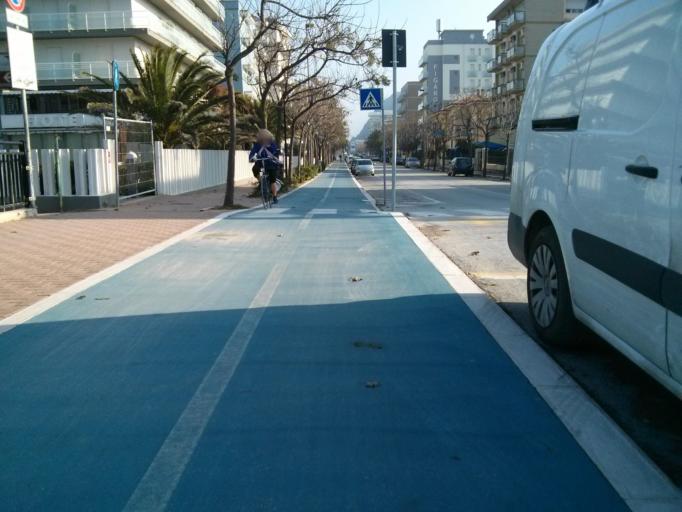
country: IT
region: The Marches
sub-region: Provincia di Pesaro e Urbino
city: Pesaro
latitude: 43.9095
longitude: 12.9239
